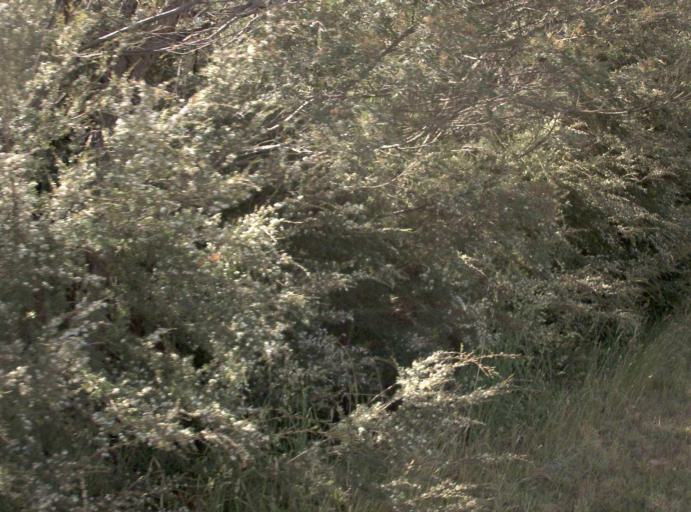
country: AU
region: Victoria
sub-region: Latrobe
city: Morwell
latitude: -38.2086
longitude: 146.4001
